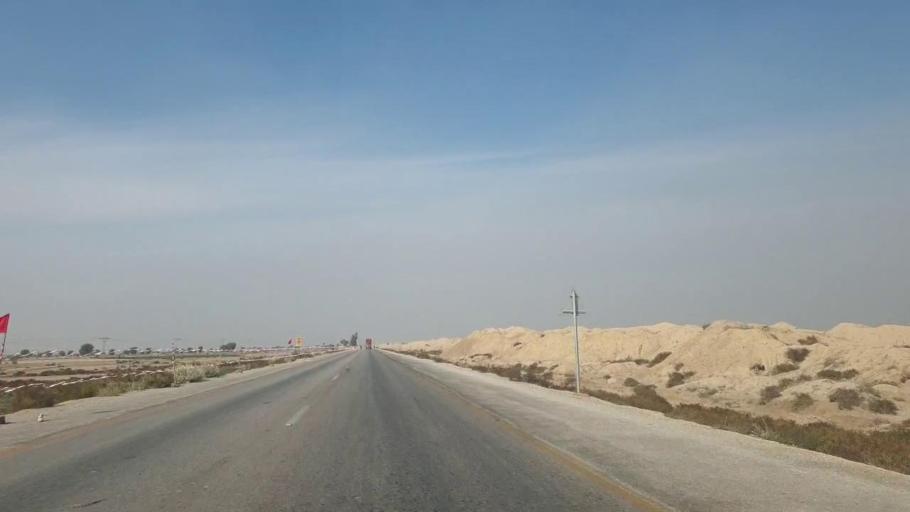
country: PK
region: Sindh
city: Sann
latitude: 25.9563
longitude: 68.1940
